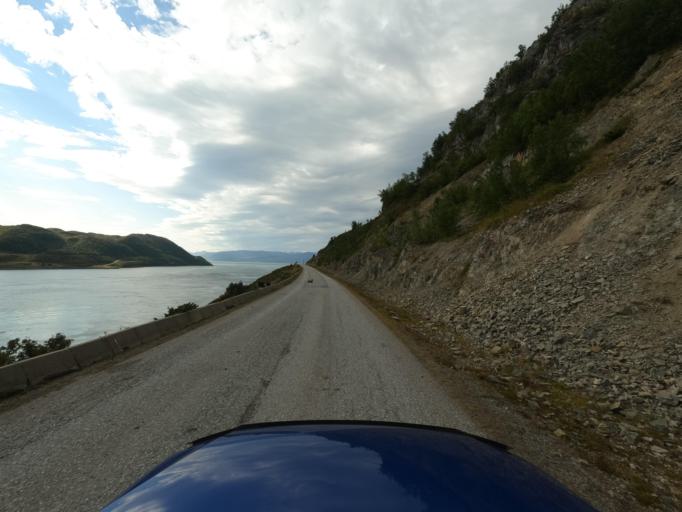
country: NO
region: Finnmark Fylke
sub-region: Kvalsund
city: Kvalsund
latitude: 70.5084
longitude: 23.9068
